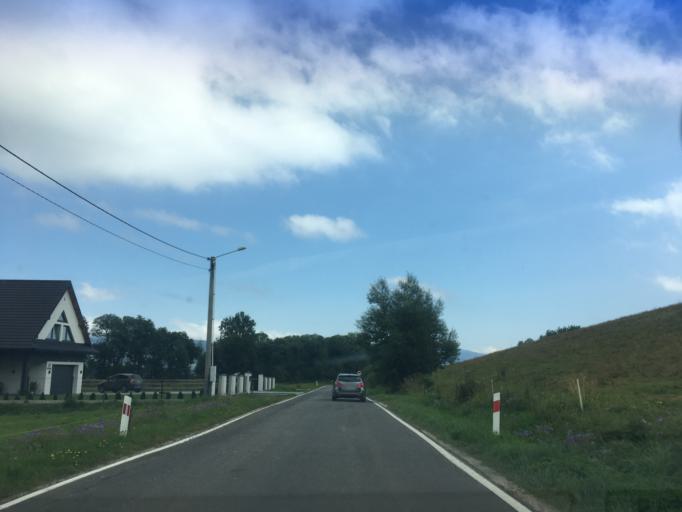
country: PL
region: Lesser Poland Voivodeship
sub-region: Powiat nowotarski
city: Frydman
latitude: 49.4390
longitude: 20.1789
